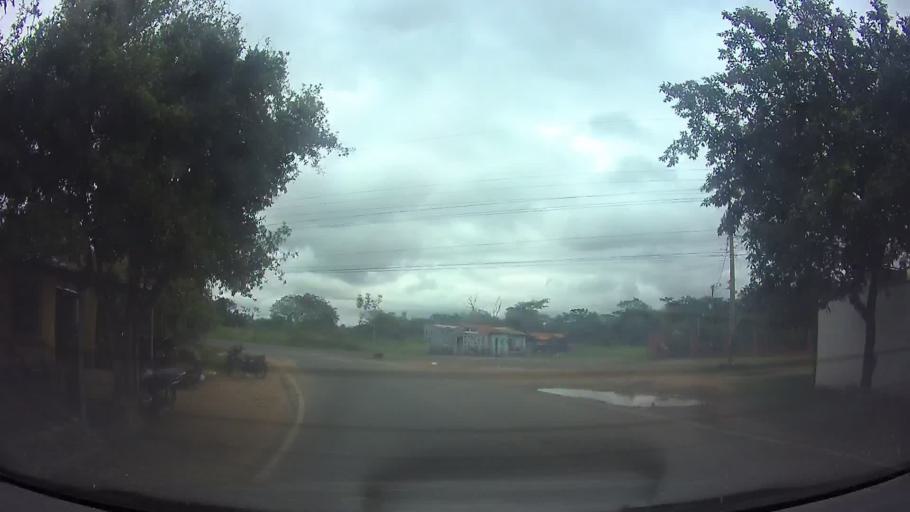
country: PY
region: Central
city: Guarambare
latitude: -25.4984
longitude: -57.4800
